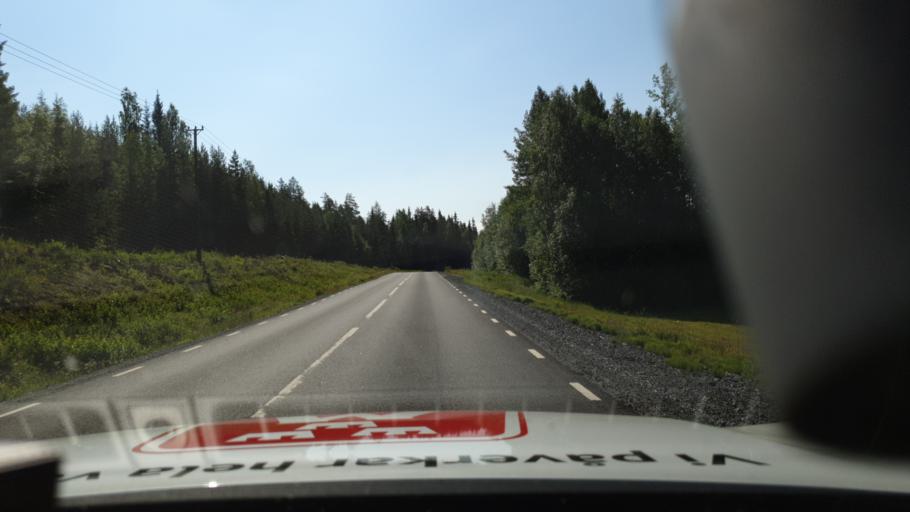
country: SE
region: Norrbotten
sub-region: Bodens Kommun
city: Saevast
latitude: 65.8280
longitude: 21.8863
